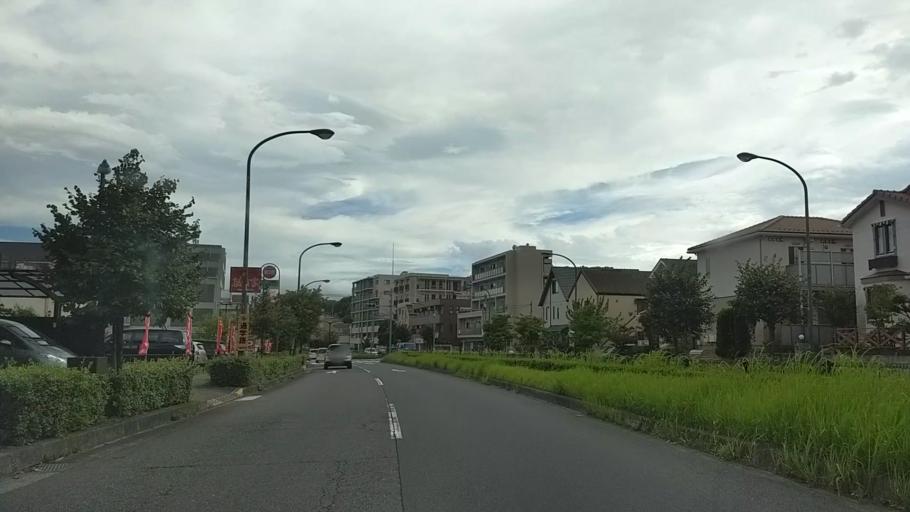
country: JP
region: Tokyo
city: Hachioji
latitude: 35.6285
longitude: 139.3274
